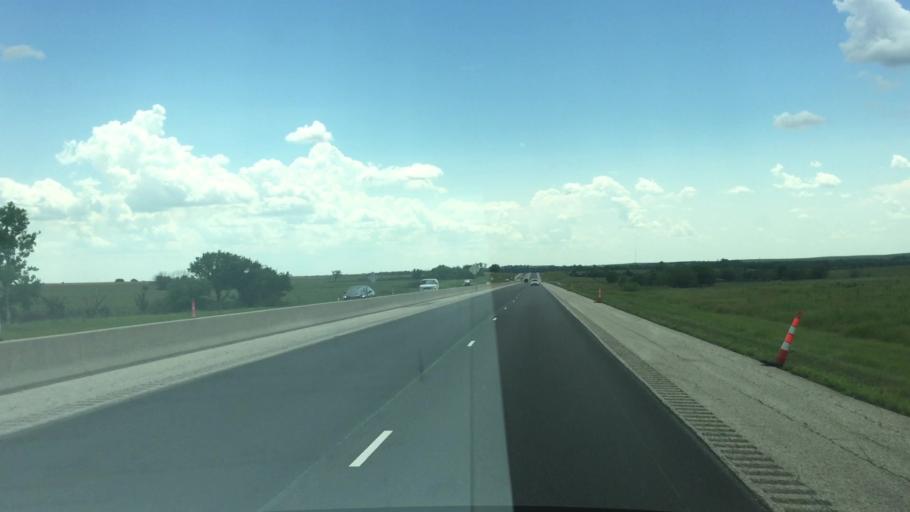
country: US
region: Kansas
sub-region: Osage County
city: Osage City
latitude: 38.6880
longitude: -95.9983
